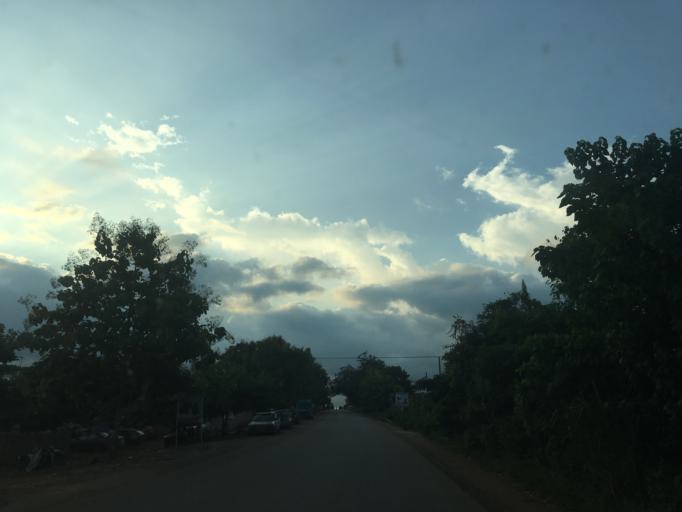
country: GH
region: Western
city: Bibiani
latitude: 6.6908
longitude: -2.4406
